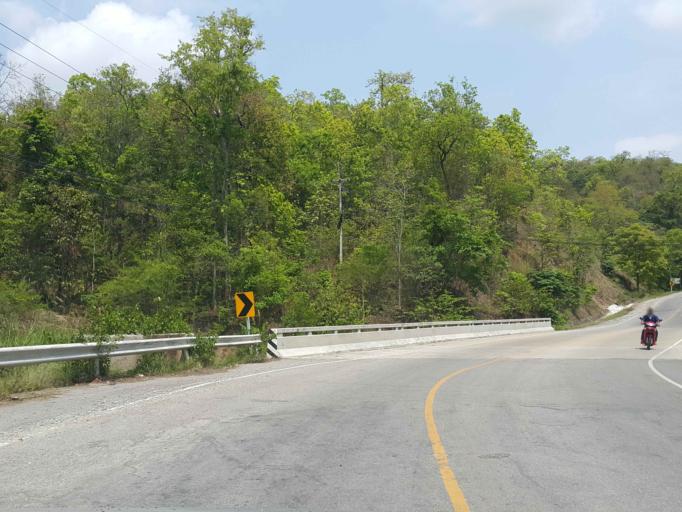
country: TH
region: Lampang
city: Thoen
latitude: 17.6413
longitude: 99.3047
